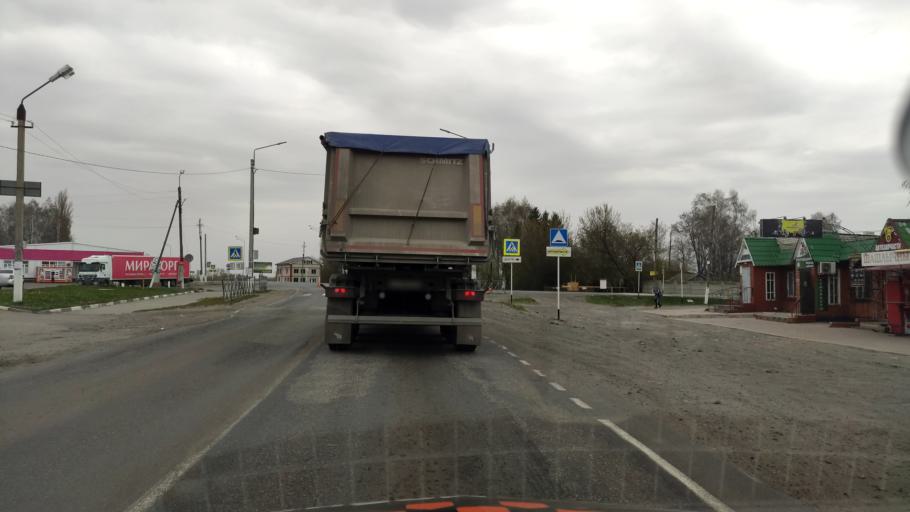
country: RU
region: Kursk
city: Gorshechnoye
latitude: 51.5226
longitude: 38.0219
